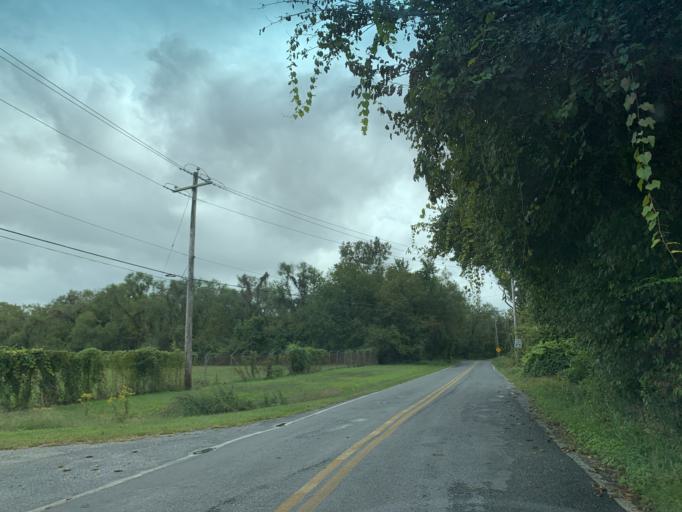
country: US
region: Maryland
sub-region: Caroline County
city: Denton
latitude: 38.8933
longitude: -75.8376
